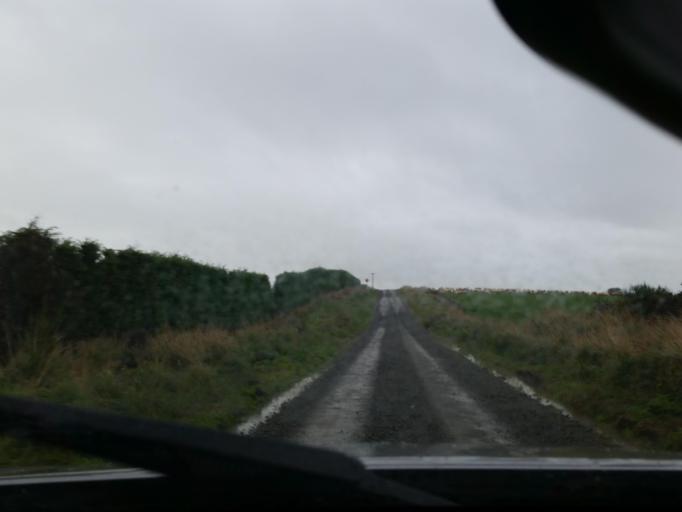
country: NZ
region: Southland
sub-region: Southland District
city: Riverton
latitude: -46.2412
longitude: 168.1164
